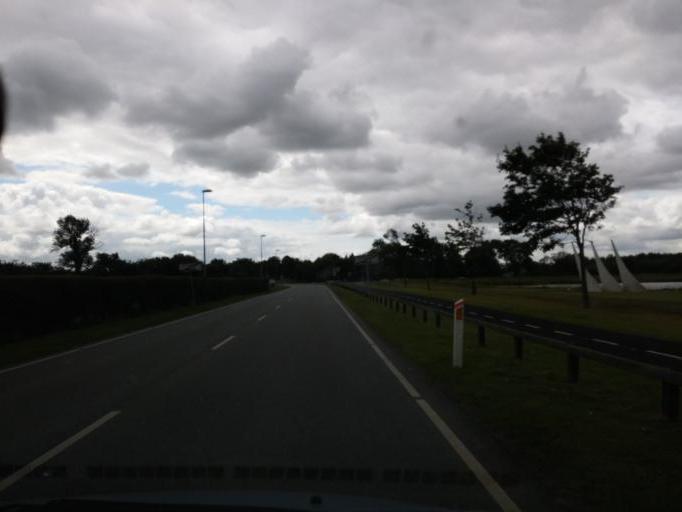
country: DK
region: South Denmark
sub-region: Kerteminde Kommune
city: Kerteminde
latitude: 55.4435
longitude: 10.6572
